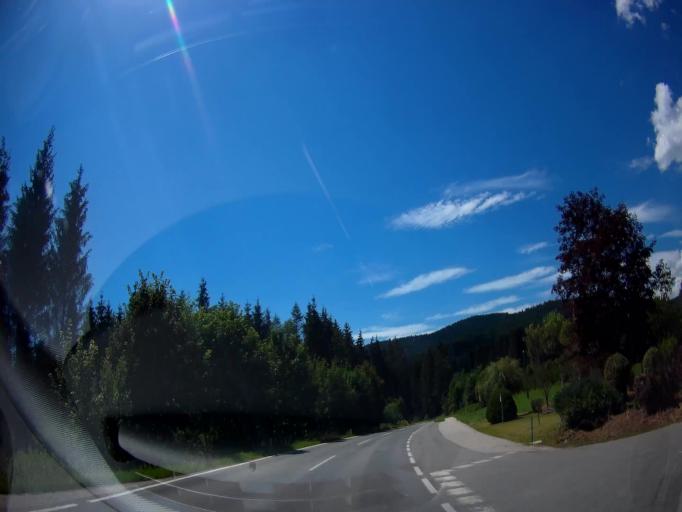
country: AT
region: Carinthia
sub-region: Politischer Bezirk Sankt Veit an der Glan
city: Gurk
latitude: 46.8679
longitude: 14.2662
